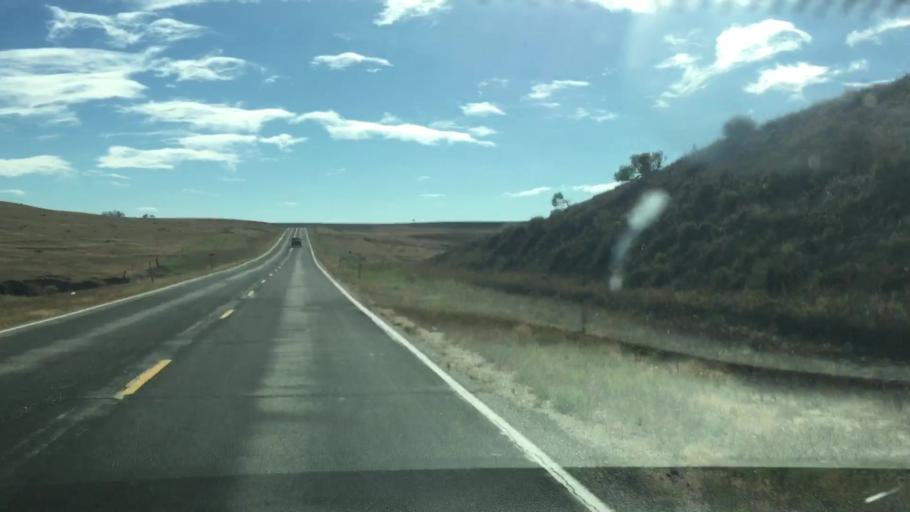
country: US
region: Colorado
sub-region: Elbert County
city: Kiowa
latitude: 39.2758
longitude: -104.2585
